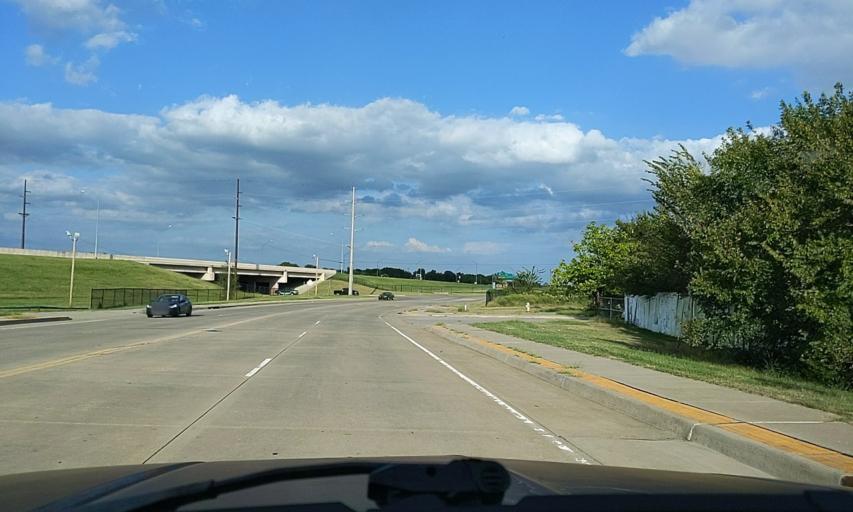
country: US
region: Oklahoma
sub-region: Tulsa County
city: Tulsa
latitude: 36.1962
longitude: -95.9772
